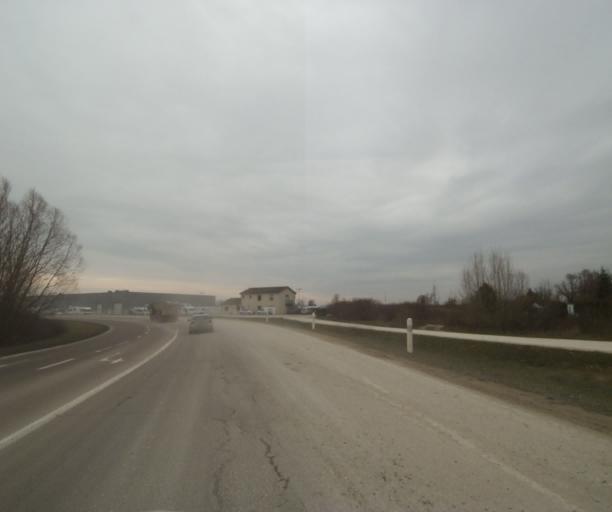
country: FR
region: Champagne-Ardenne
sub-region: Departement de la Haute-Marne
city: Villiers-en-Lieu
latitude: 48.6433
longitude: 4.9091
